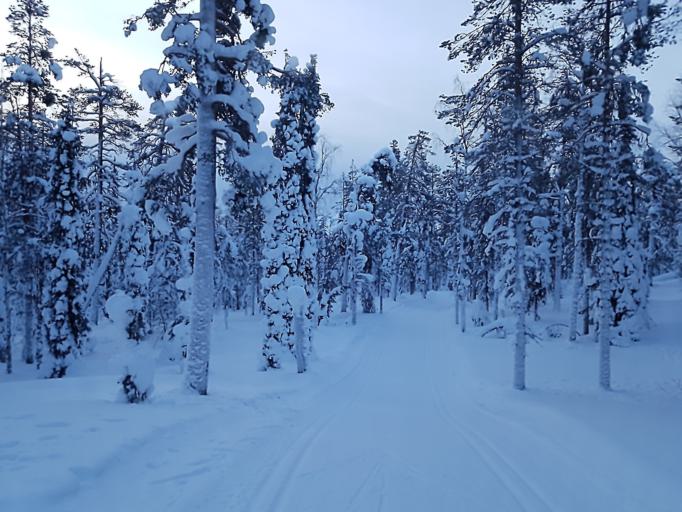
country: FI
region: Lapland
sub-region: Tunturi-Lappi
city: Kolari
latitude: 67.6430
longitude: 24.2327
